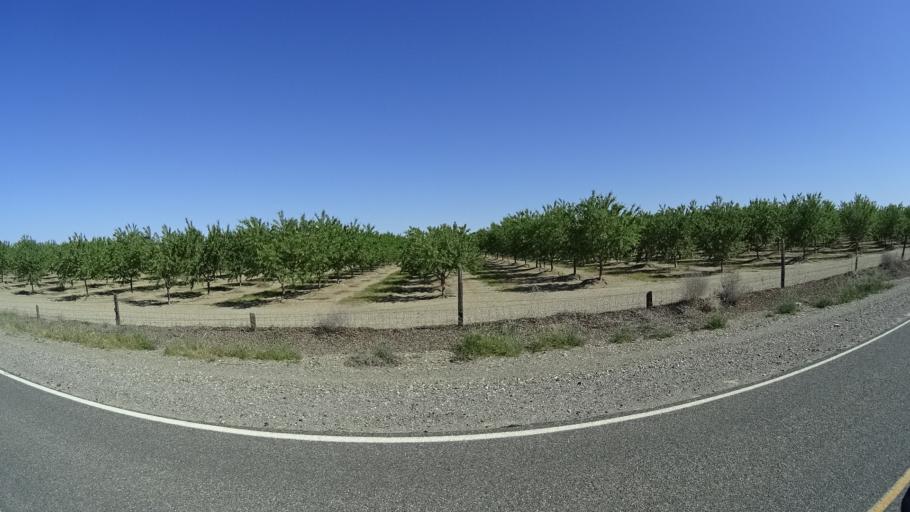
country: US
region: California
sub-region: Glenn County
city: Willows
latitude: 39.6239
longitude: -122.1553
